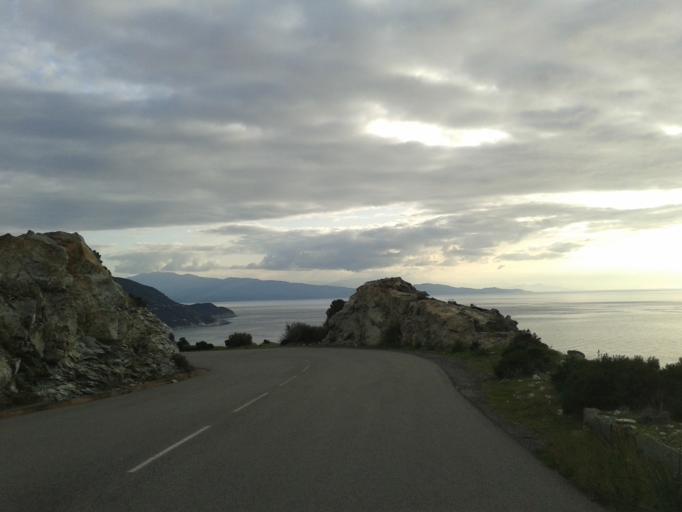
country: FR
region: Corsica
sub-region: Departement de la Haute-Corse
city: Brando
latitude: 42.8729
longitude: 9.3335
